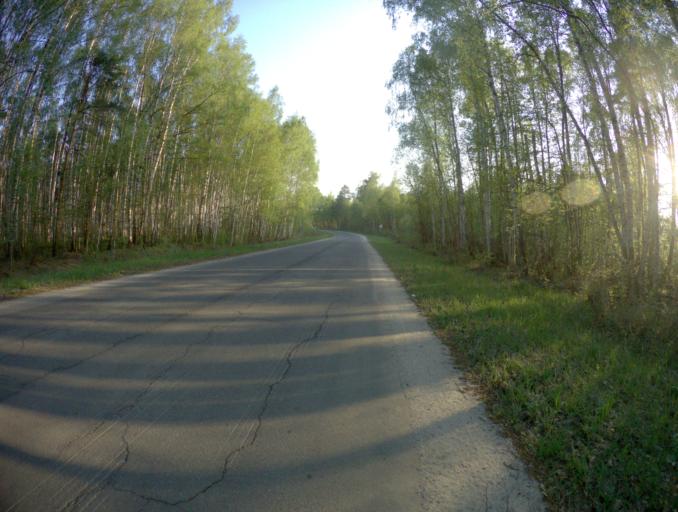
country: RU
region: Vladimir
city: Vyazniki
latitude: 56.3313
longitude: 42.1247
